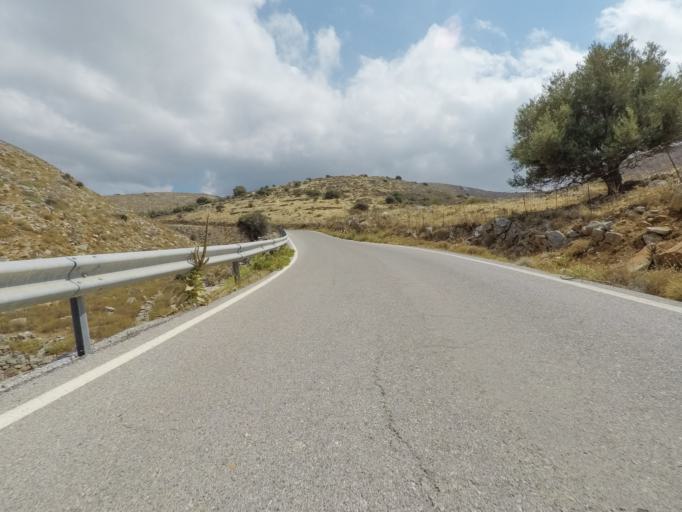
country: GR
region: Crete
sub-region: Nomos Lasithiou
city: Elounda
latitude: 35.3120
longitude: 25.6772
